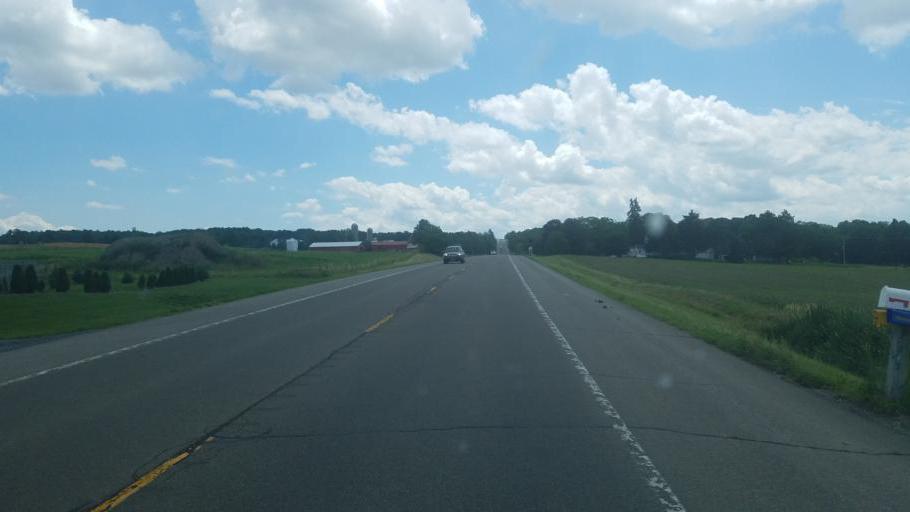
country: US
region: New York
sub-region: Yates County
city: Keuka Park
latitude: 42.6017
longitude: -77.0377
